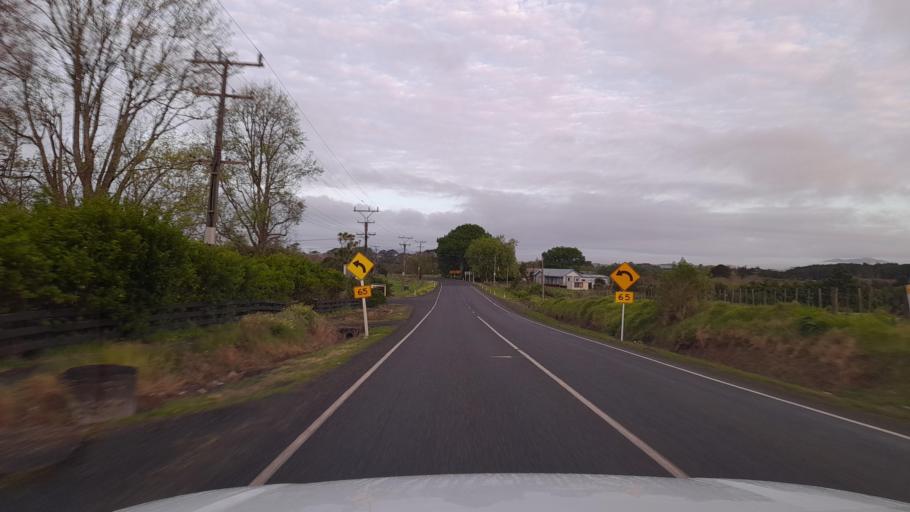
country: NZ
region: Northland
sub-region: Whangarei
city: Maungatapere
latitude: -35.7387
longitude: 174.1405
